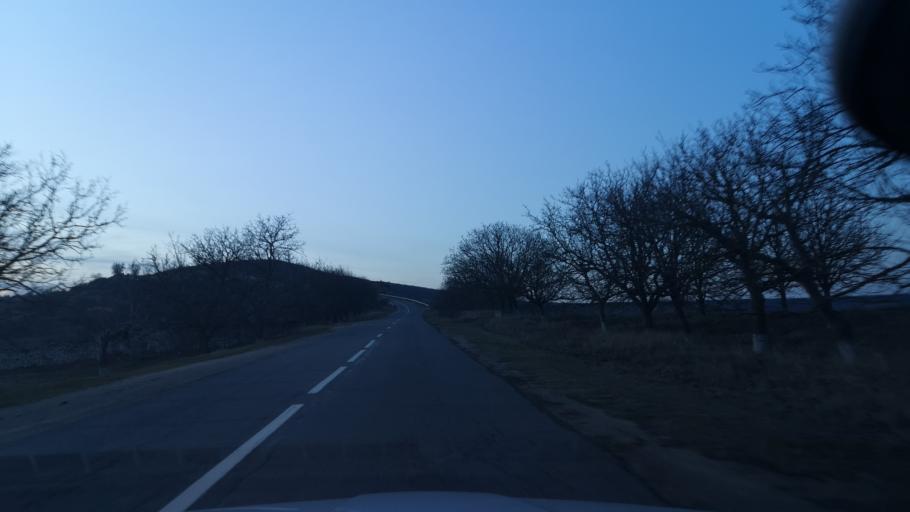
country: MD
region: Telenesti
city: Cocieri
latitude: 47.3095
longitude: 28.9734
